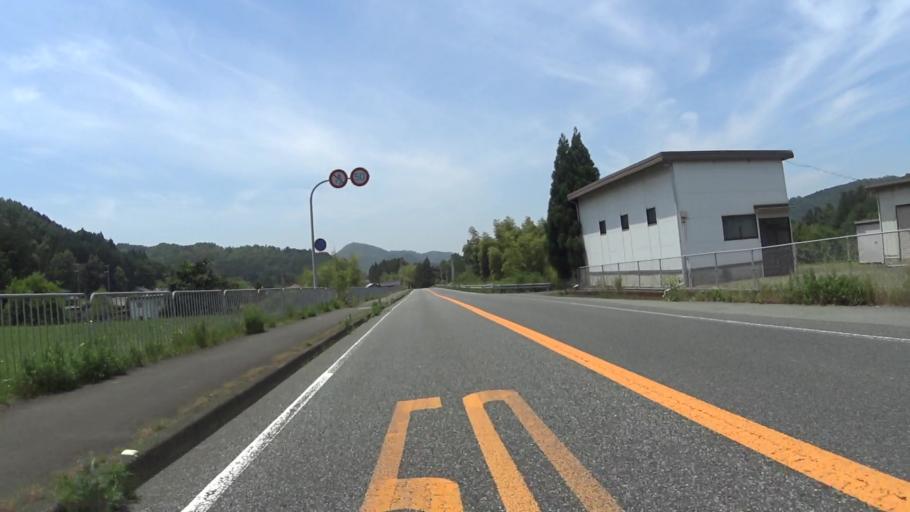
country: JP
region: Kyoto
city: Ayabe
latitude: 35.2099
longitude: 135.2448
